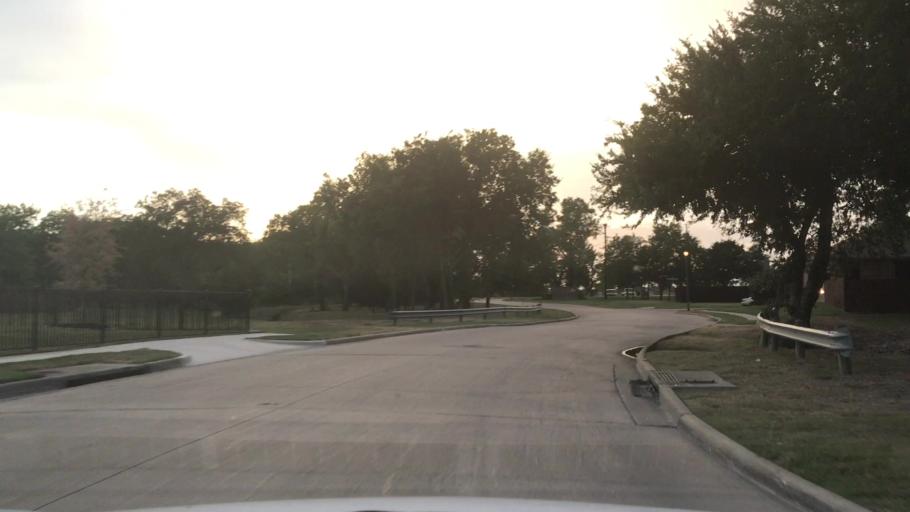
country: US
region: Texas
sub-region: Dallas County
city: Seagoville
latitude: 32.6926
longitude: -96.5523
